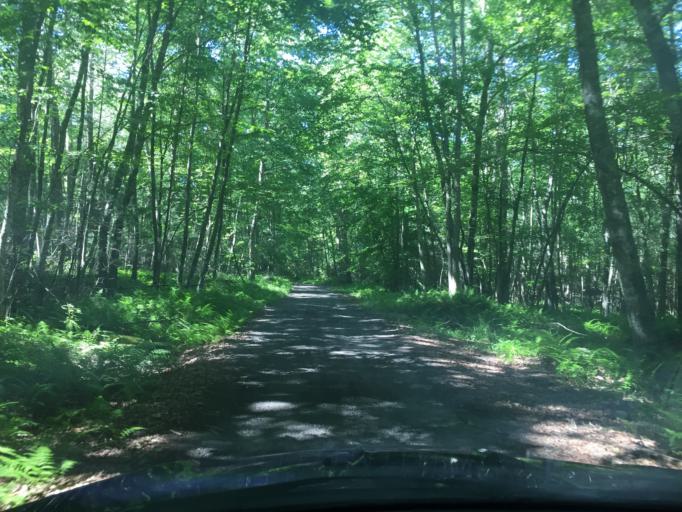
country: US
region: Rhode Island
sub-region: Washington County
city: Hopkinton
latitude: 41.5202
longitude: -71.8014
